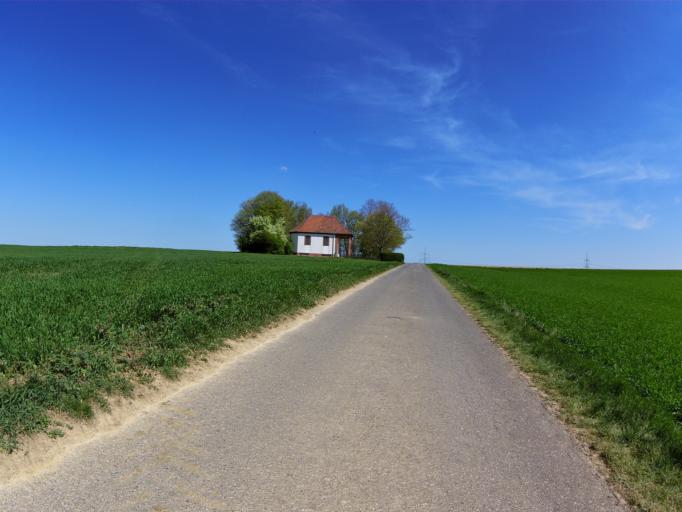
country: DE
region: Bavaria
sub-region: Regierungsbezirk Unterfranken
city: Rottendorf
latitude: 49.7940
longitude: 10.0454
